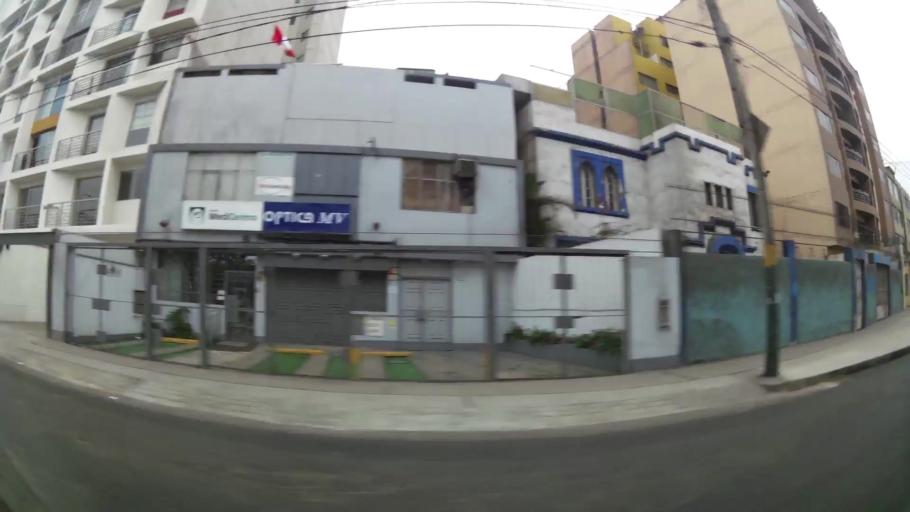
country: PE
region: Lima
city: Lima
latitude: -12.0726
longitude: -77.0619
